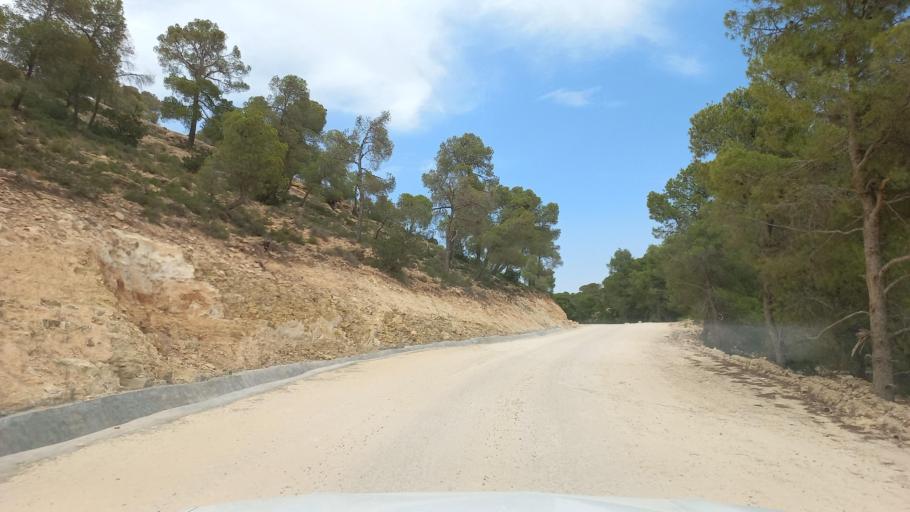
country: TN
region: Al Qasrayn
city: Kasserine
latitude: 35.3791
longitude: 8.8819
